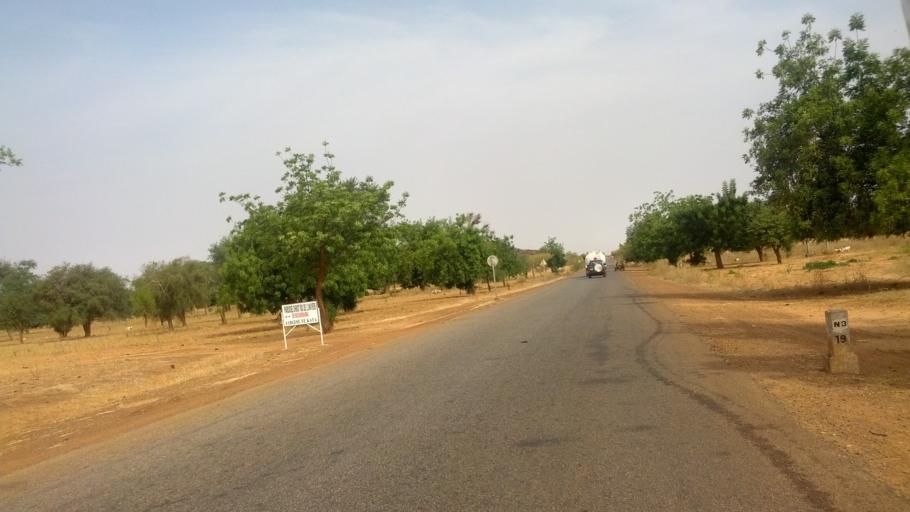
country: BF
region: Centre-Nord
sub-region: Province du Sanmatenga
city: Kaya
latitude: 12.9155
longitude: -1.0779
